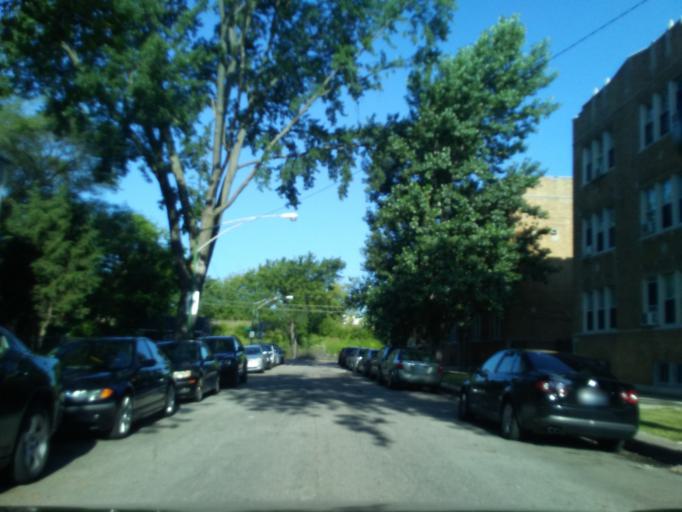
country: US
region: Illinois
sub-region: Cook County
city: Oak Park
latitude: 41.9335
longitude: -87.7409
